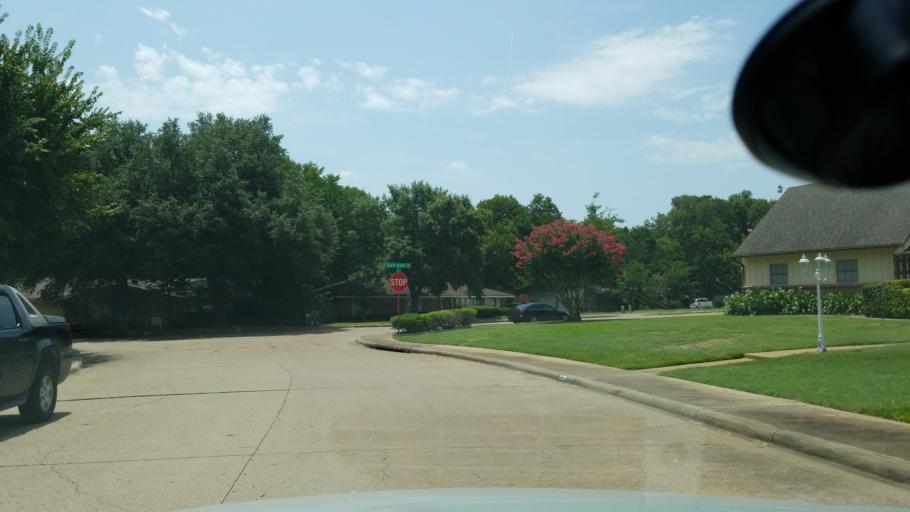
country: US
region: Texas
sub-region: Dallas County
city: Duncanville
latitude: 32.6780
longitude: -96.8355
